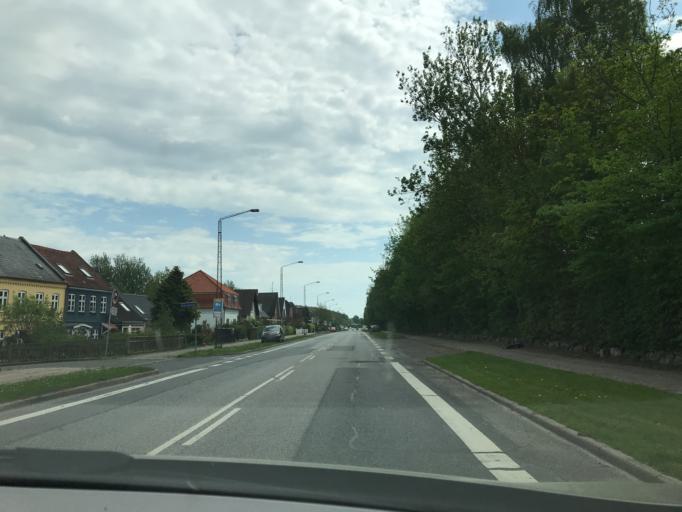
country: DK
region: South Denmark
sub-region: Assens Kommune
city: Assens
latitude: 55.2641
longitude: 9.9055
